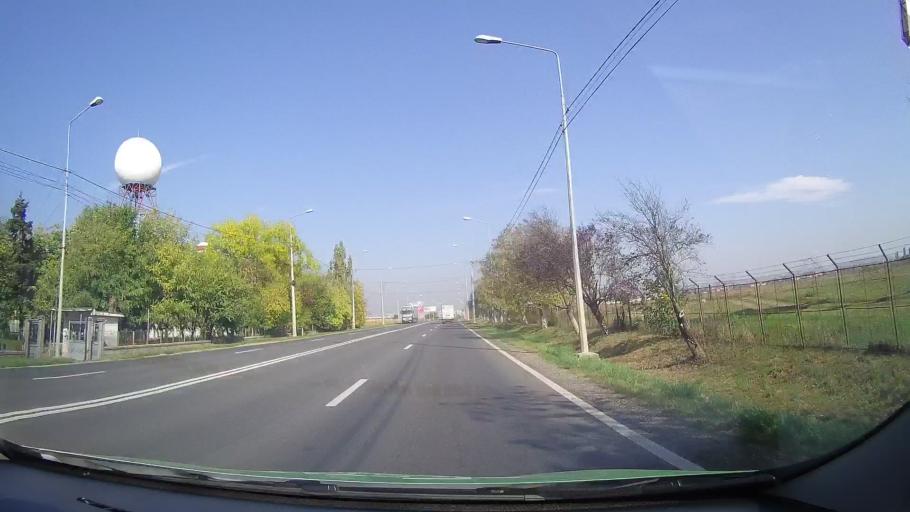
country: RO
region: Bihor
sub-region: Comuna Biharea
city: Oradea
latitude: 47.0349
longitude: 21.8993
